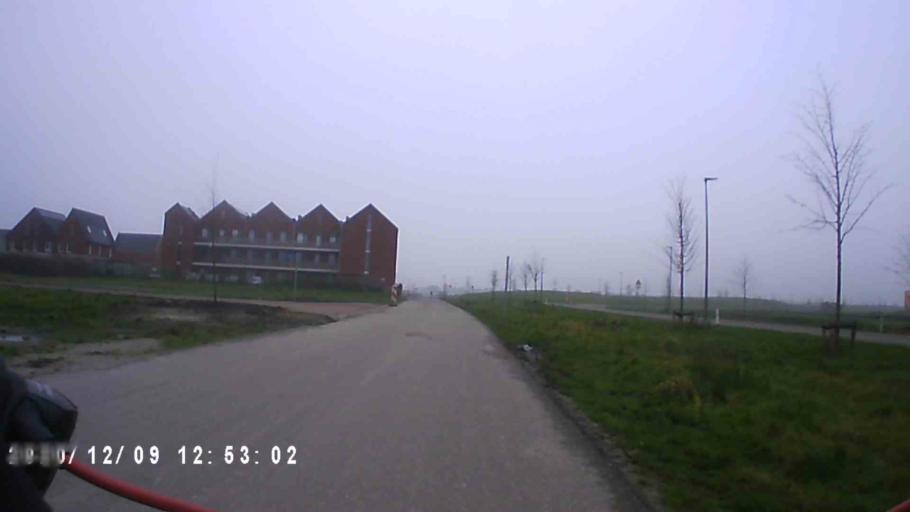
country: NL
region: Groningen
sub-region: Gemeente Groningen
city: Oosterpark
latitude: 53.2328
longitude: 6.6549
